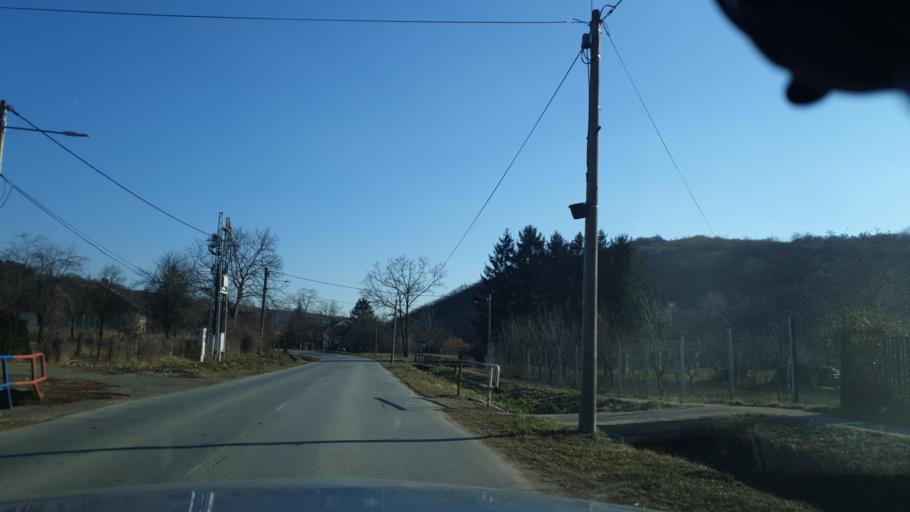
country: RS
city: Vrdnik
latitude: 45.1161
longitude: 19.7950
